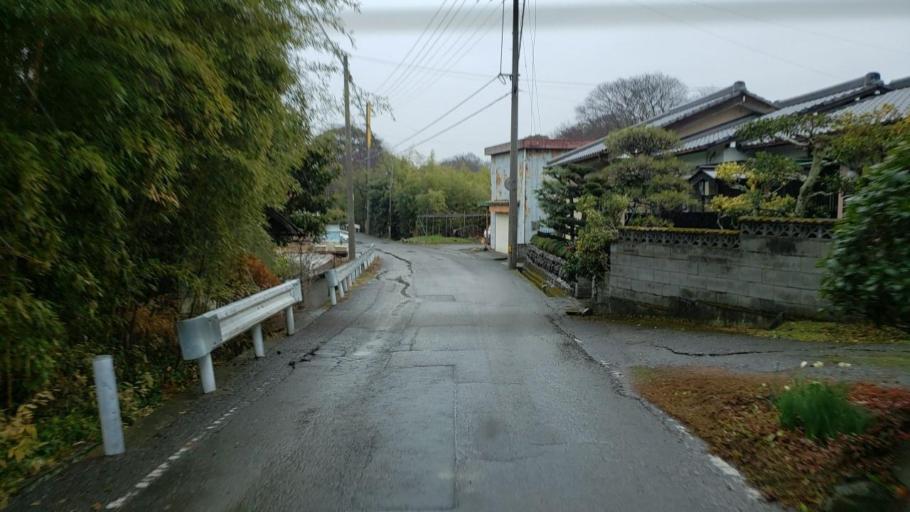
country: JP
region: Tokushima
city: Wakimachi
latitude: 34.0777
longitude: 134.2494
